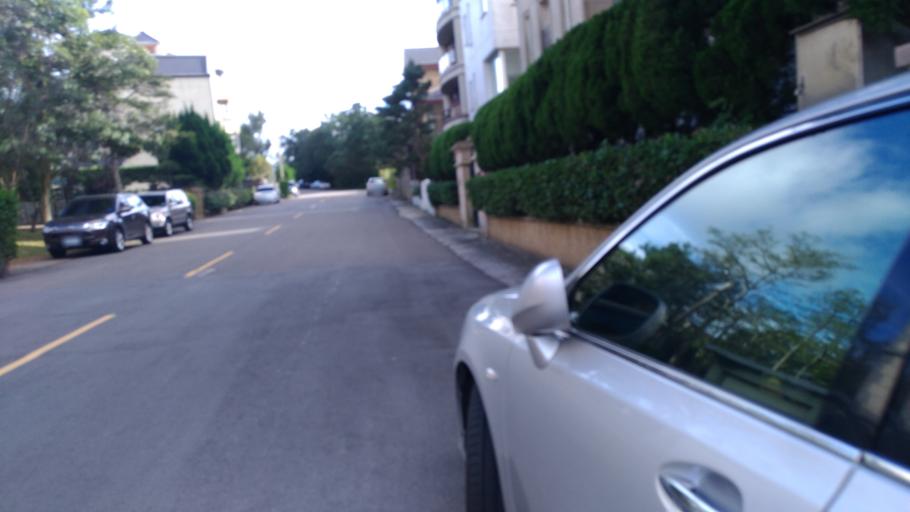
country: TW
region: Taiwan
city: Daxi
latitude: 24.8841
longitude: 121.1713
